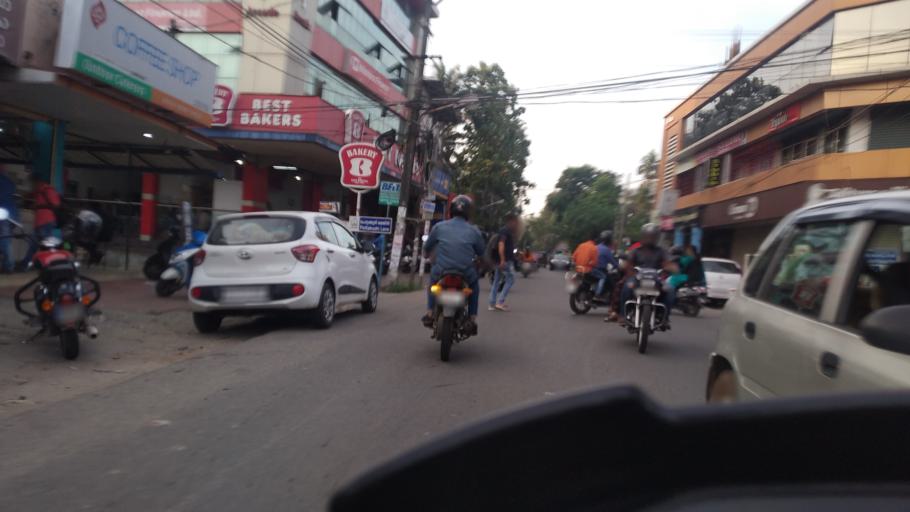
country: IN
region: Kerala
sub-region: Ernakulam
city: Elur
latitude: 10.0054
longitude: 76.2888
